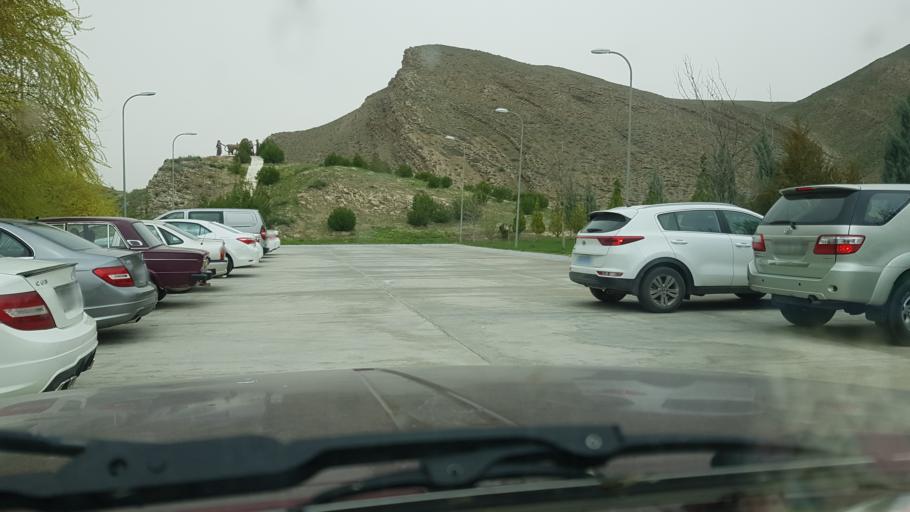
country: TM
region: Ahal
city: Arcabil
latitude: 38.0241
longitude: 58.0062
